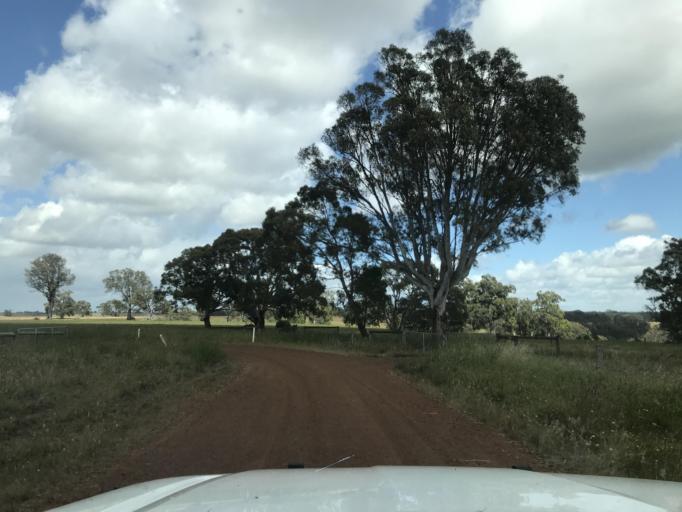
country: AU
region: South Australia
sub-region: Wattle Range
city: Penola
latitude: -37.1938
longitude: 141.4183
